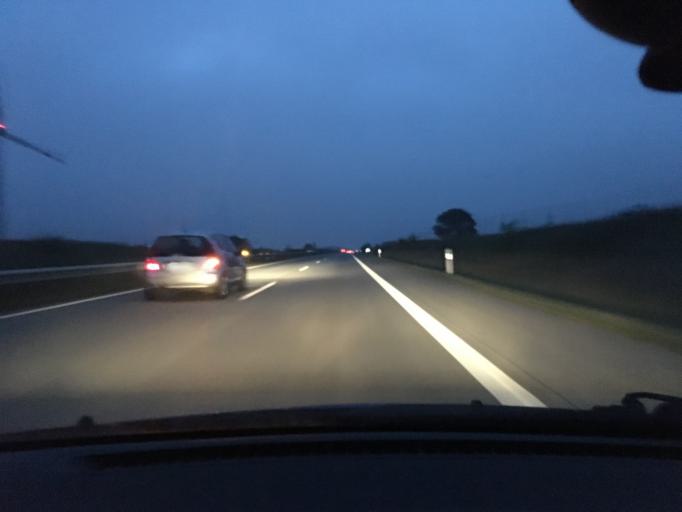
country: DE
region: Schleswig-Holstein
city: Nienbuttel
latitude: 54.0433
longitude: 9.4116
